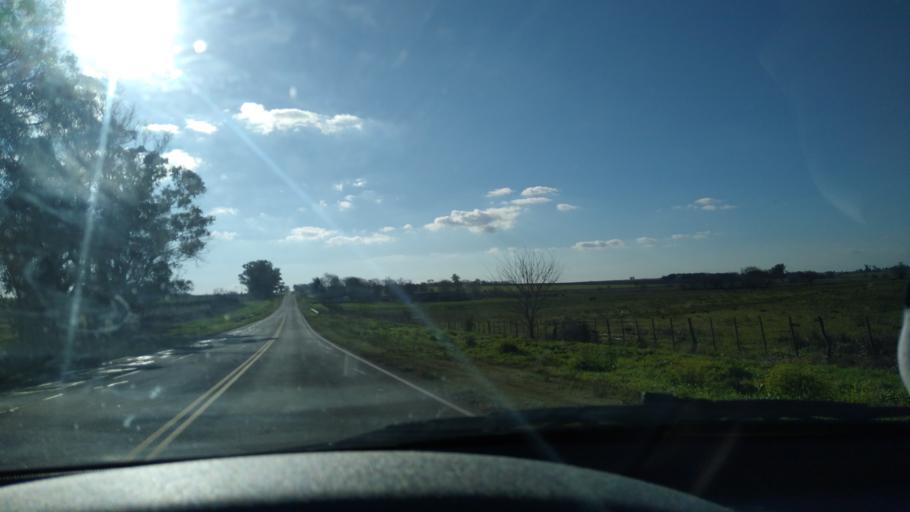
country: AR
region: Entre Rios
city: Diamante
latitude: -32.1166
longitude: -60.5714
